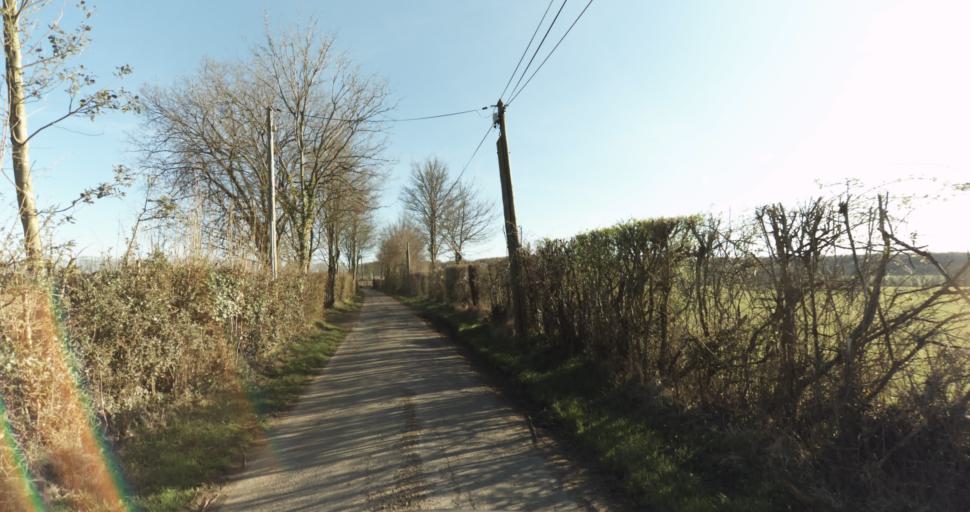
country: FR
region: Lower Normandy
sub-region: Departement du Calvados
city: Livarot
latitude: 48.9824
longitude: 0.0858
